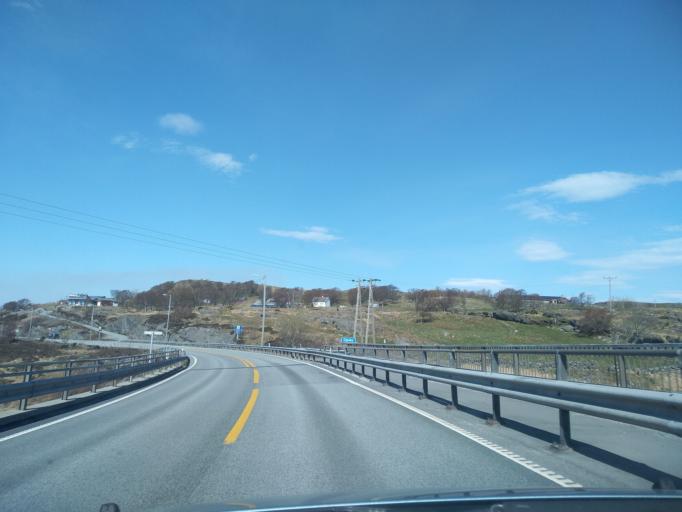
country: NO
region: Rogaland
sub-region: Bokn
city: Bokn
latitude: 59.2532
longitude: 5.4725
